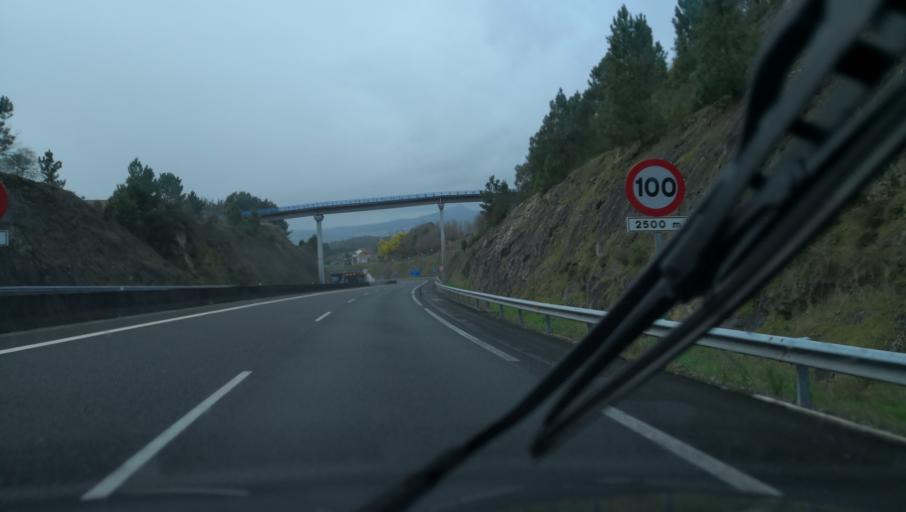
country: ES
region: Galicia
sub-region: Provincia da Coruna
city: Ribeira
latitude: 42.7492
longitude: -8.3893
